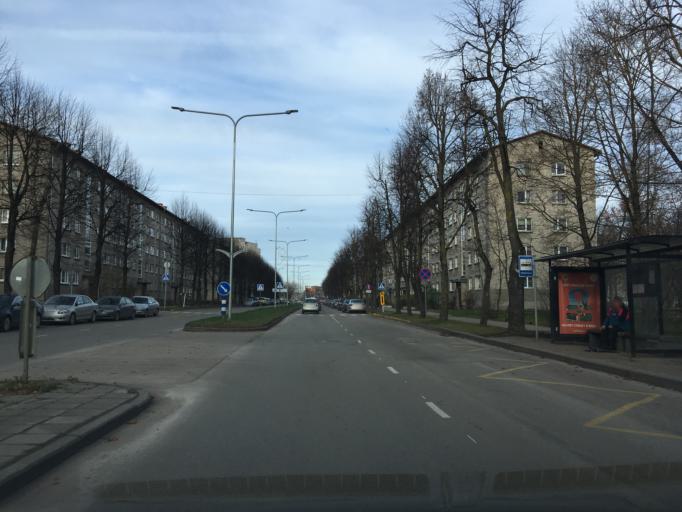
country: EE
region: Ida-Virumaa
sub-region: Narva linn
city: Narva
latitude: 59.3762
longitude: 28.1812
